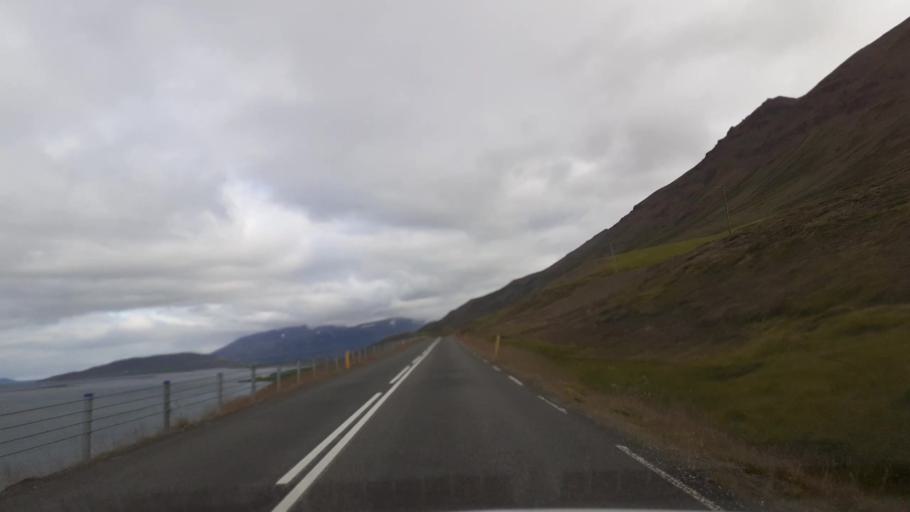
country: IS
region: Northeast
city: Akureyri
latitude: 65.8401
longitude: -18.0563
